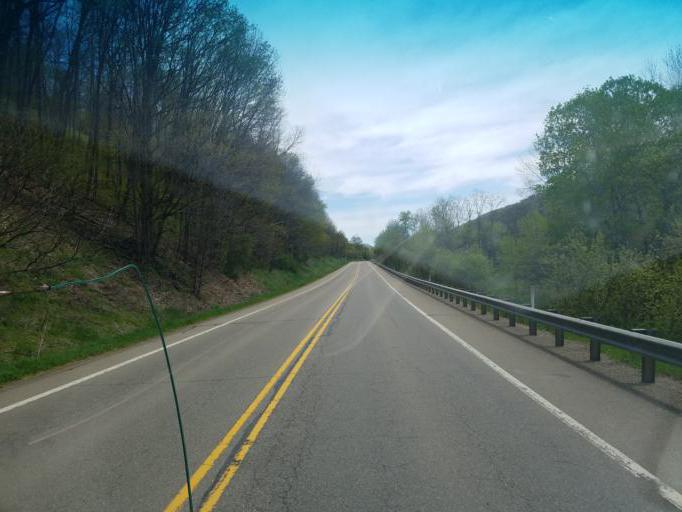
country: US
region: Pennsylvania
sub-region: Potter County
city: Galeton
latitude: 41.7385
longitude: -77.6335
